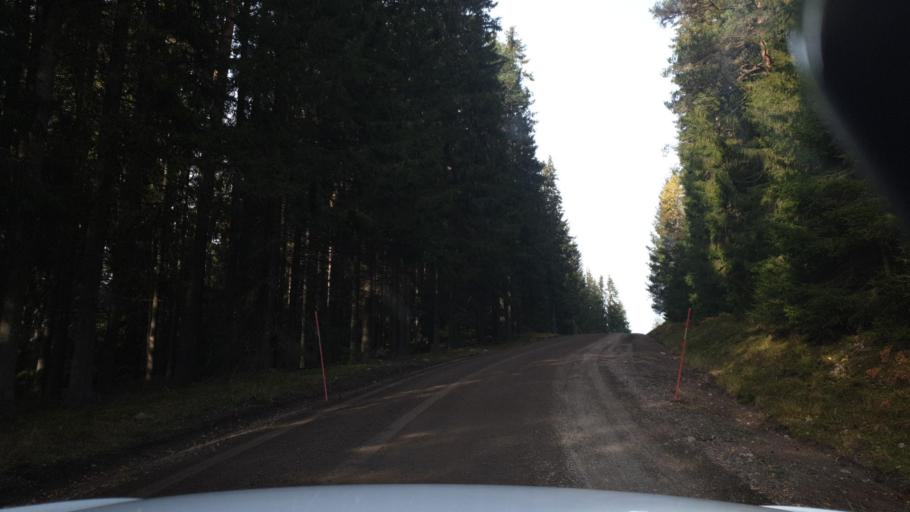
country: NO
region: Hedmark
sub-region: Eidskog
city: Skotterud
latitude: 59.7396
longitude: 12.0774
